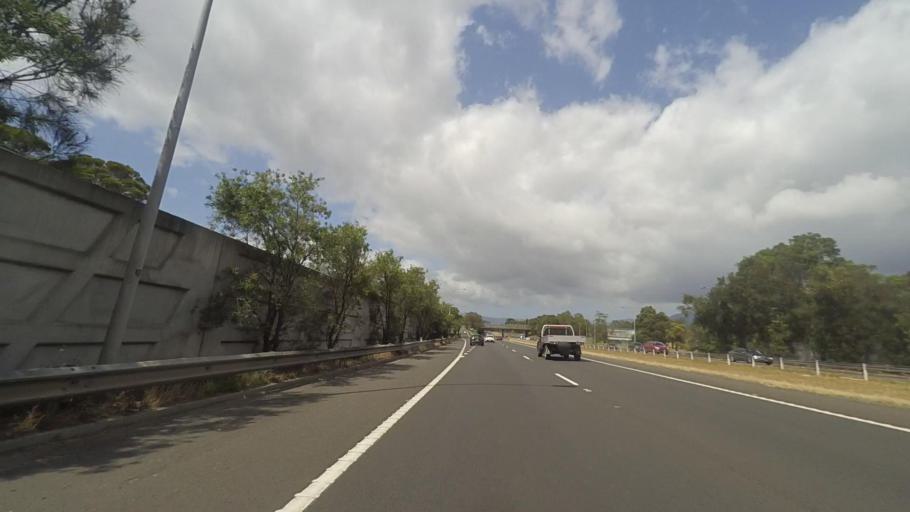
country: AU
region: New South Wales
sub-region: Wollongong
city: Koonawarra
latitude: -34.4971
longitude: 150.7991
